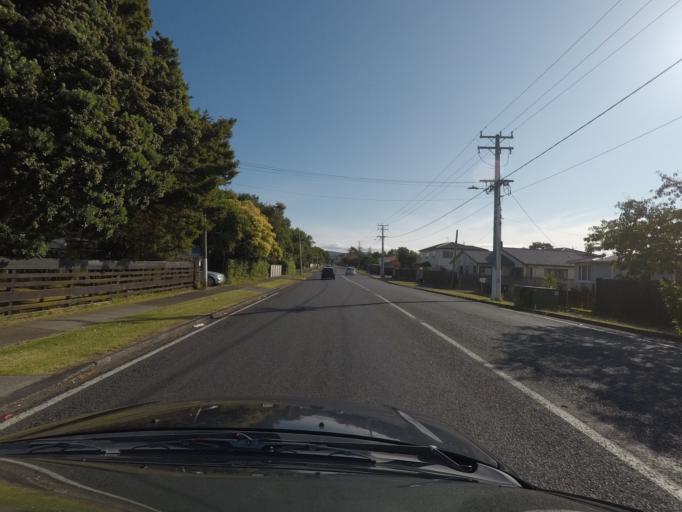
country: NZ
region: Auckland
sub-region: Auckland
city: Rosebank
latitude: -36.8632
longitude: 174.6107
